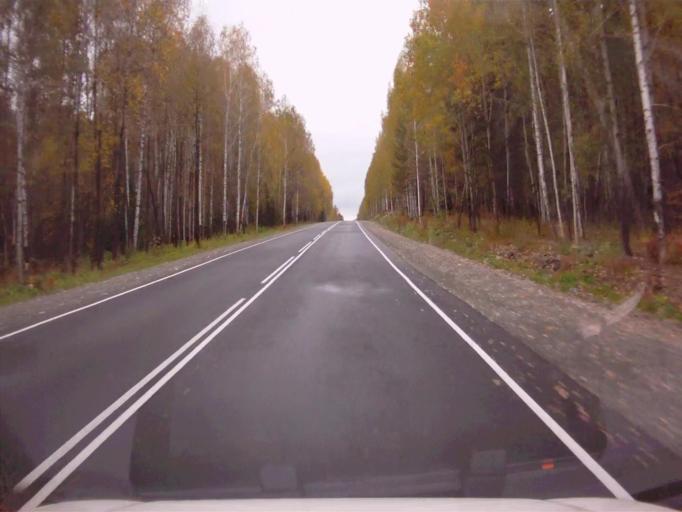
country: RU
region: Chelyabinsk
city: Nyazepetrovsk
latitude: 56.0647
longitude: 59.7030
